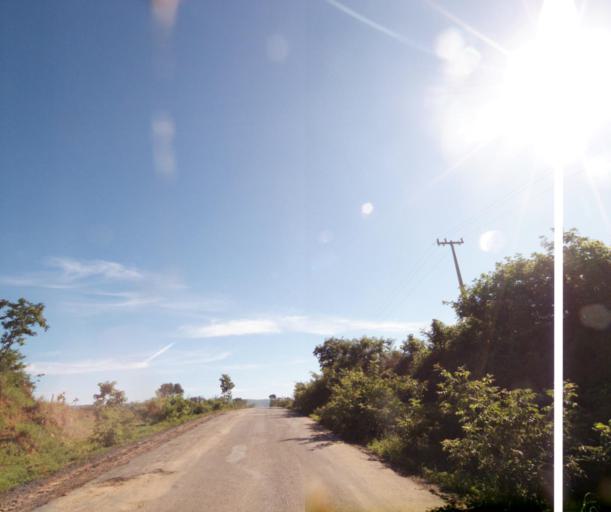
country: BR
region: Bahia
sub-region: Sao Felix Do Coribe
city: Santa Maria da Vitoria
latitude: -13.6359
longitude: -44.4333
